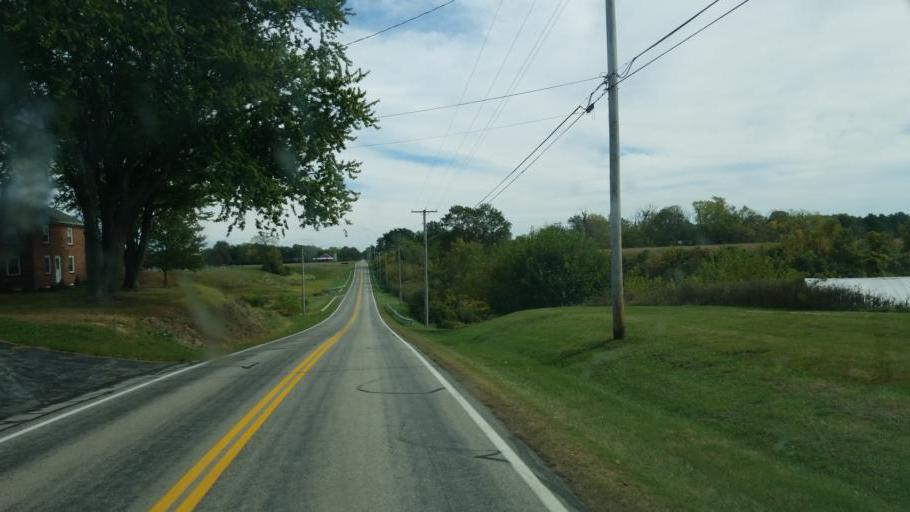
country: US
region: Ohio
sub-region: Erie County
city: Huron
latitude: 41.3648
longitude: -82.4876
